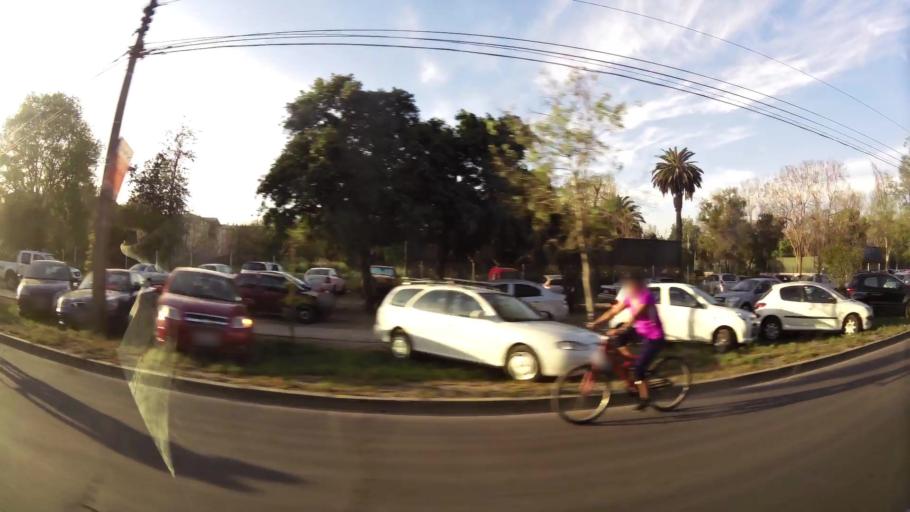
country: CL
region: Santiago Metropolitan
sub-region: Provincia de Santiago
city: Lo Prado
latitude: -33.4442
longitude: -70.6873
